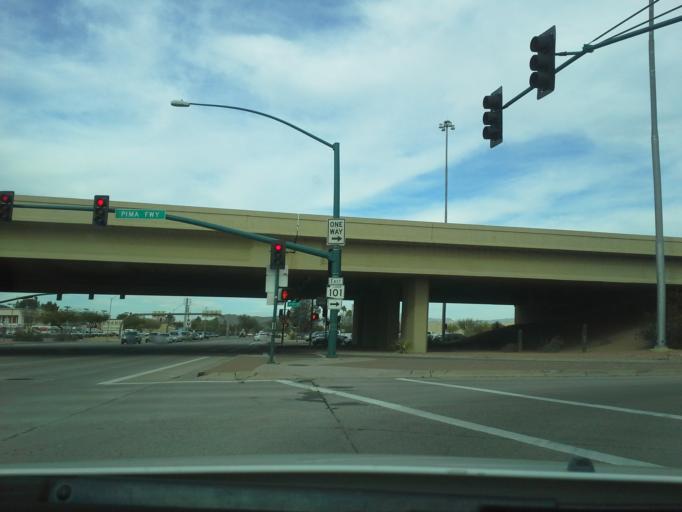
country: US
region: Arizona
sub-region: Maricopa County
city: Paradise Valley
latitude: 33.6715
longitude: -112.0309
